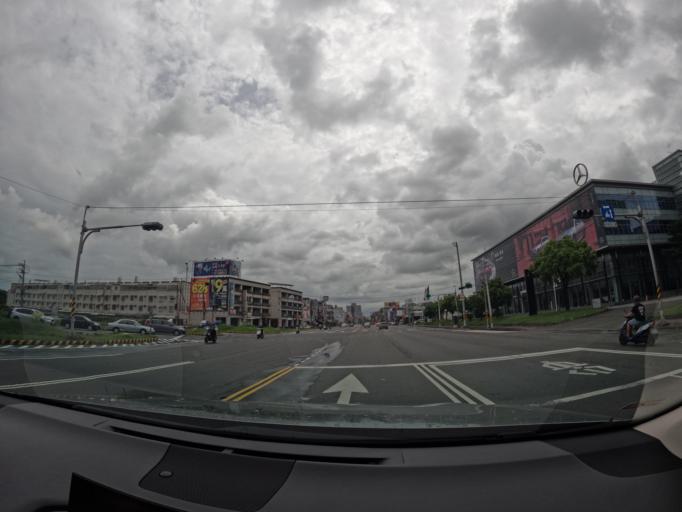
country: TW
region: Taiwan
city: Fengshan
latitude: 22.6335
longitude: 120.3883
